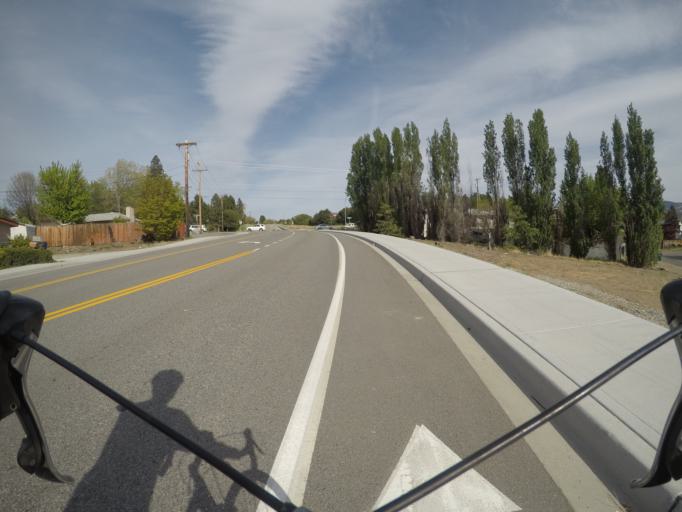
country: US
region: Washington
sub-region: Douglas County
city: East Wenatchee
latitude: 47.4126
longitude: -120.2829
